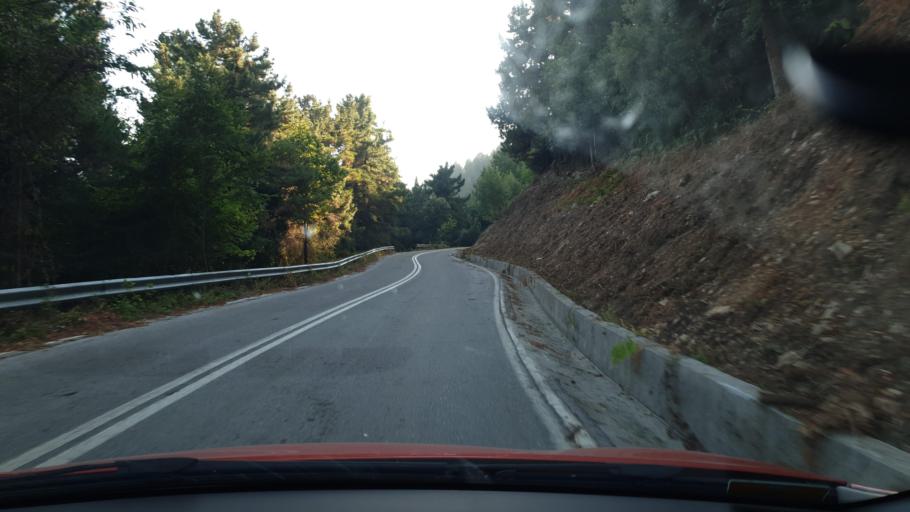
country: GR
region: Central Greece
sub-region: Nomos Evvoias
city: Kymi
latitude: 38.6326
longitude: 23.9345
